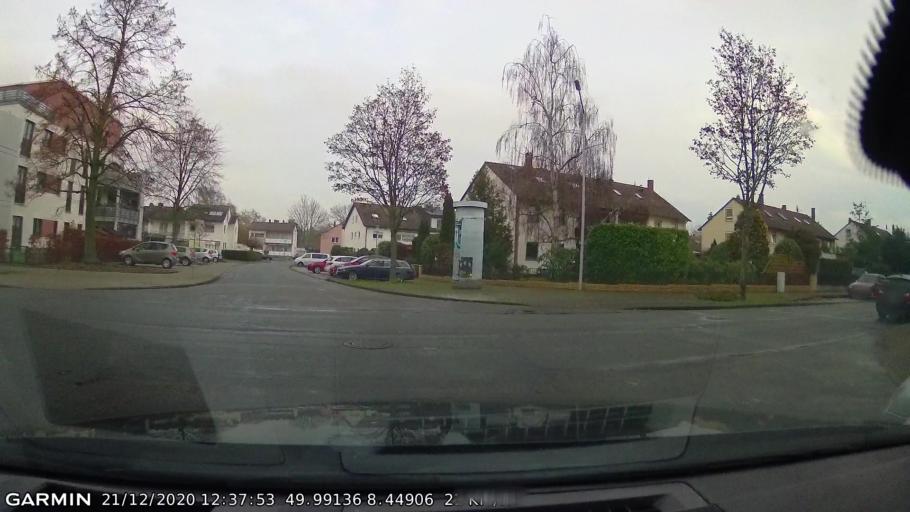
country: DE
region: Hesse
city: Raunheim
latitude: 49.9913
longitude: 8.4485
